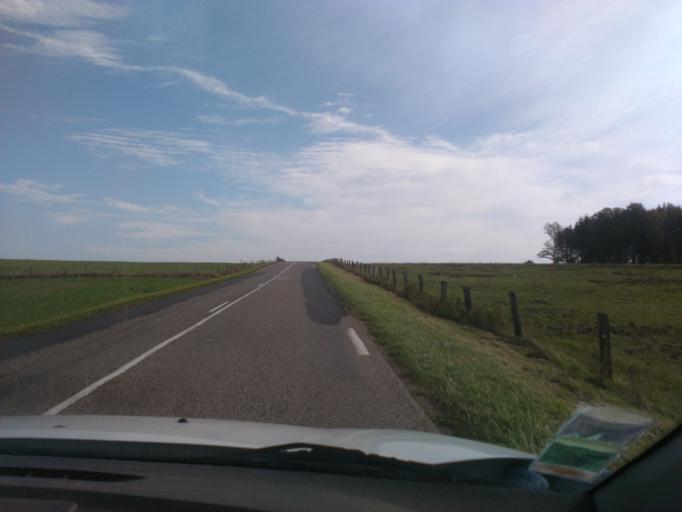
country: FR
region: Lorraine
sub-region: Departement des Vosges
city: Rambervillers
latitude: 48.3553
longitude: 6.5677
